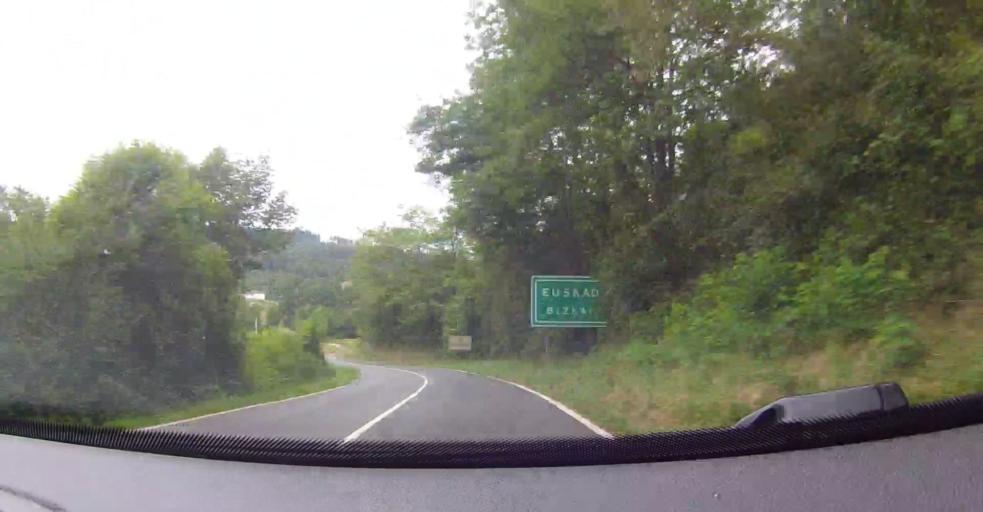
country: ES
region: Basque Country
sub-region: Bizkaia
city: Balmaseda
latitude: 43.2435
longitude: -3.2546
